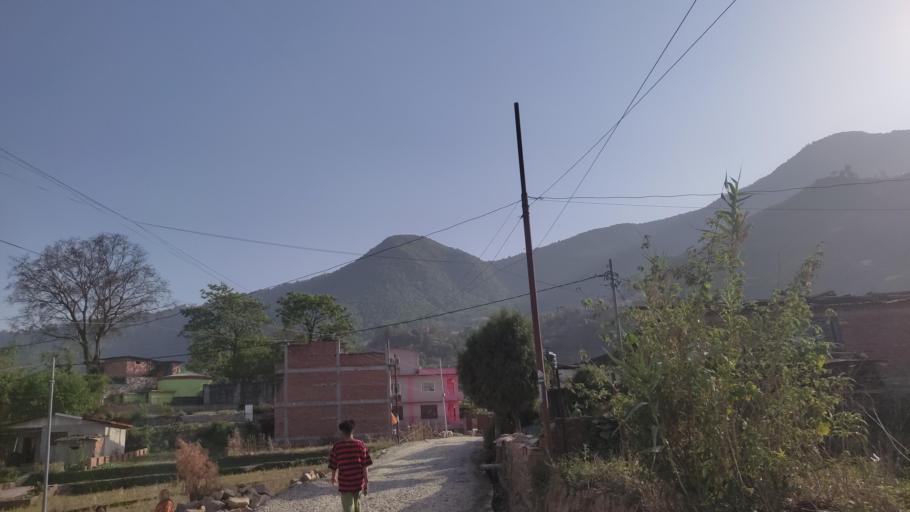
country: NP
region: Central Region
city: Kirtipur
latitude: 27.6549
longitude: 85.2764
